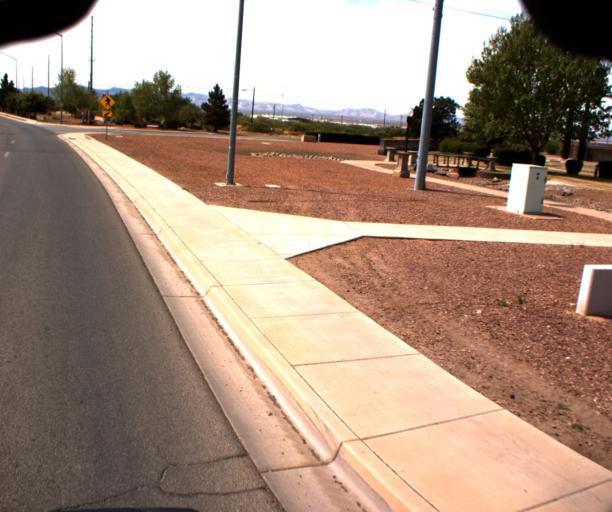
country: US
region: Arizona
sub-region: Cochise County
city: Douglas
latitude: 31.3492
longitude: -109.5555
